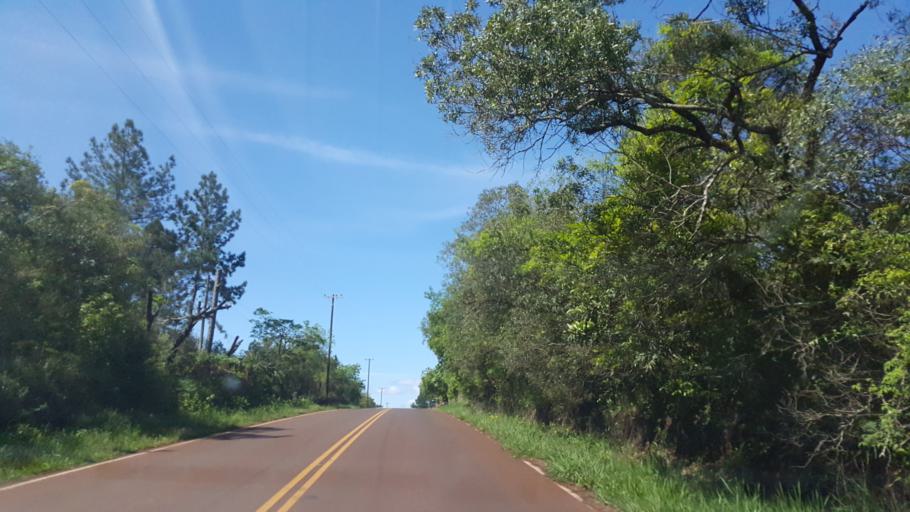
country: AR
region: Misiones
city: Garupa
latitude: -27.5032
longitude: -55.8516
